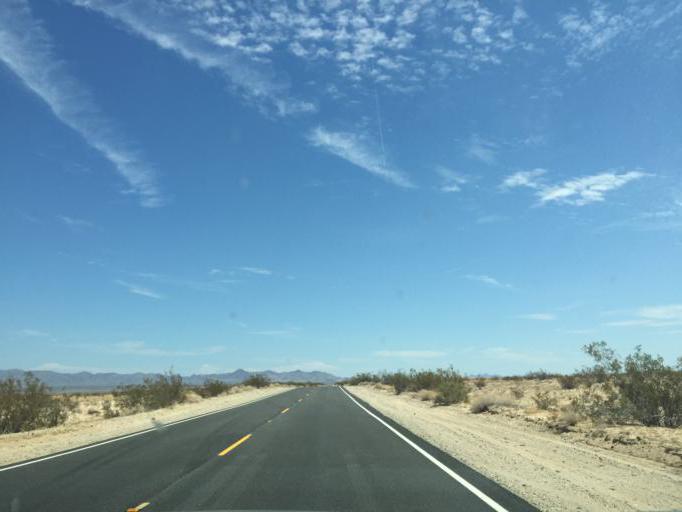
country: US
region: California
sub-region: Riverside County
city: Mesa Verde
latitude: 34.0960
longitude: -115.0369
